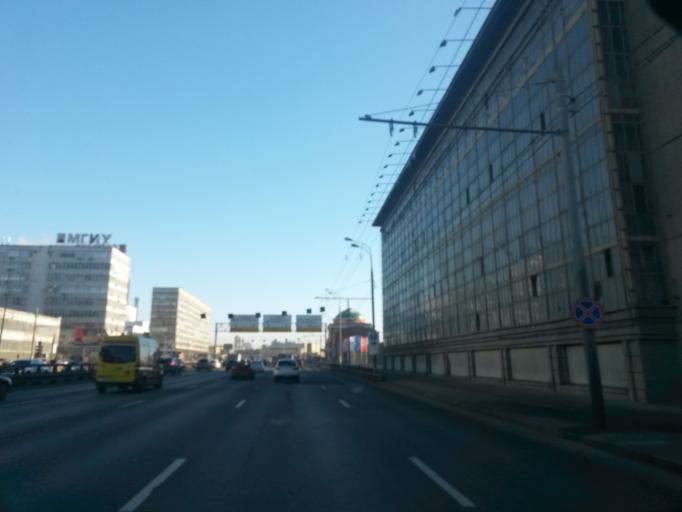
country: RU
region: Moskovskaya
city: Kozhukhovo
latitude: 55.7039
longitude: 37.6423
